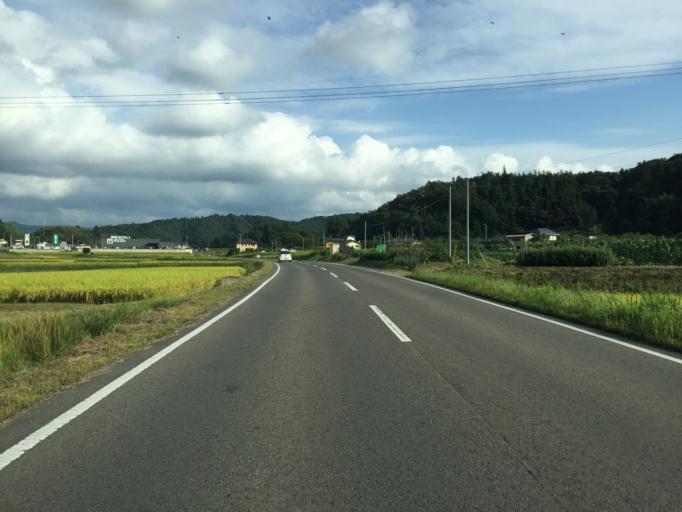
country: JP
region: Fukushima
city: Fukushima-shi
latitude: 37.6710
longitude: 140.5678
